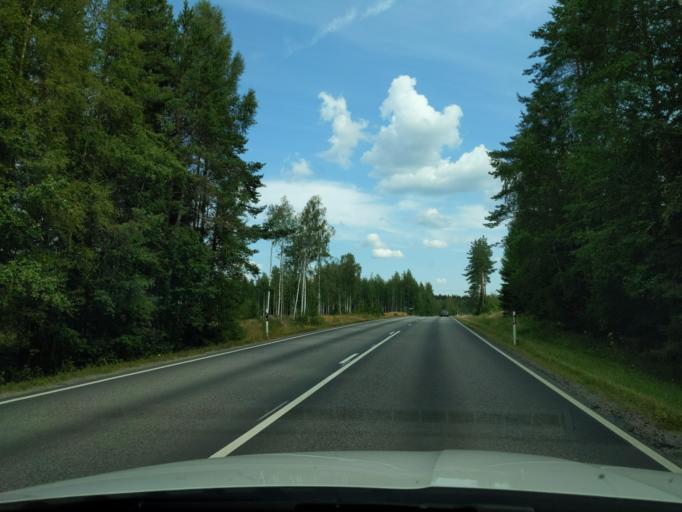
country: FI
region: Haeme
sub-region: Haemeenlinna
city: Tuulos
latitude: 61.1113
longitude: 24.8817
